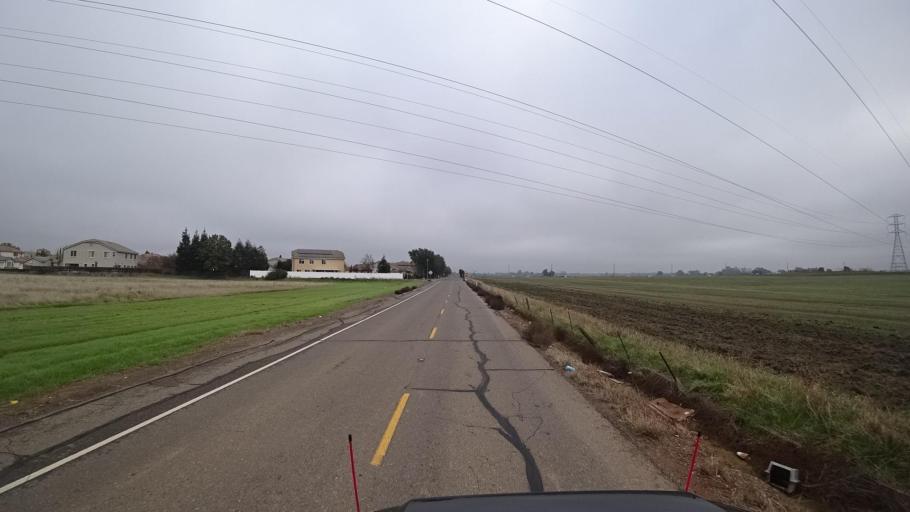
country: US
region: California
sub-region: Sacramento County
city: Elk Grove
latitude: 38.3910
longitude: -121.3514
